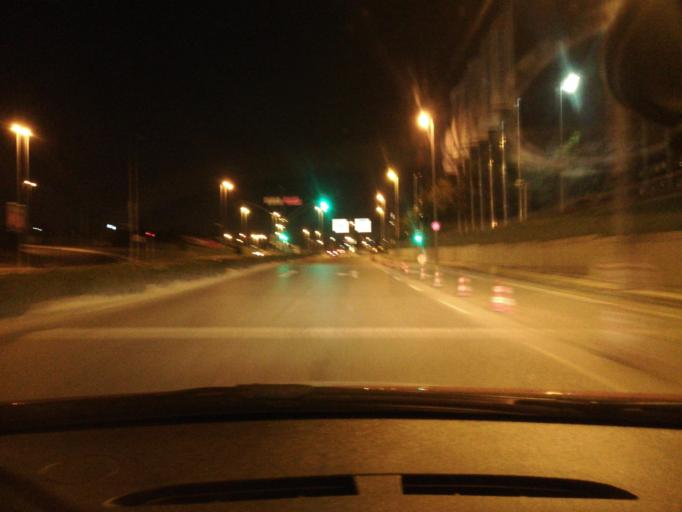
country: TR
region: Istanbul
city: Bahcelievler
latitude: 40.9818
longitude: 28.8254
